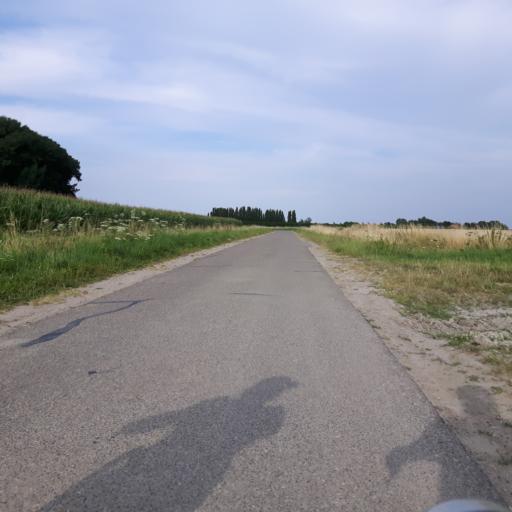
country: NL
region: Zeeland
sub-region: Gemeente Goes
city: Goes
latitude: 51.4794
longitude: 3.9273
